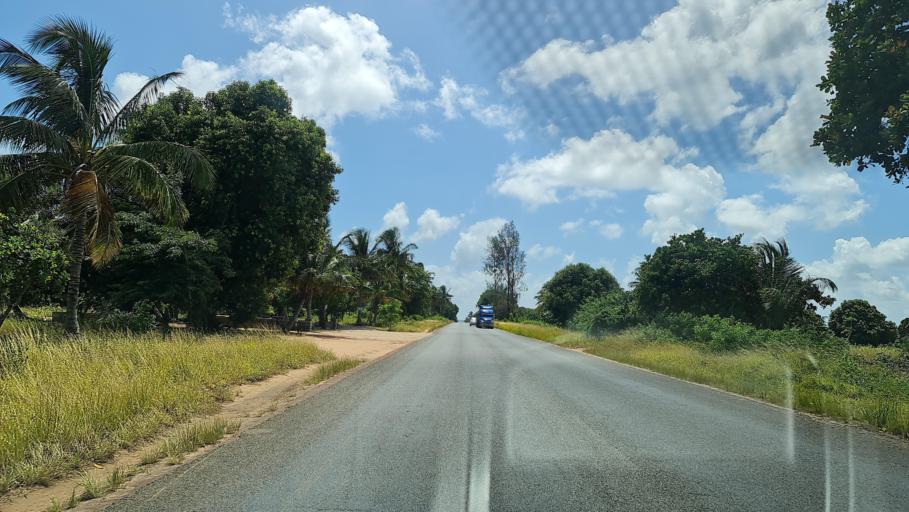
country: MZ
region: Inhambane
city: Maxixe
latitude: -24.5274
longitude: 34.9551
